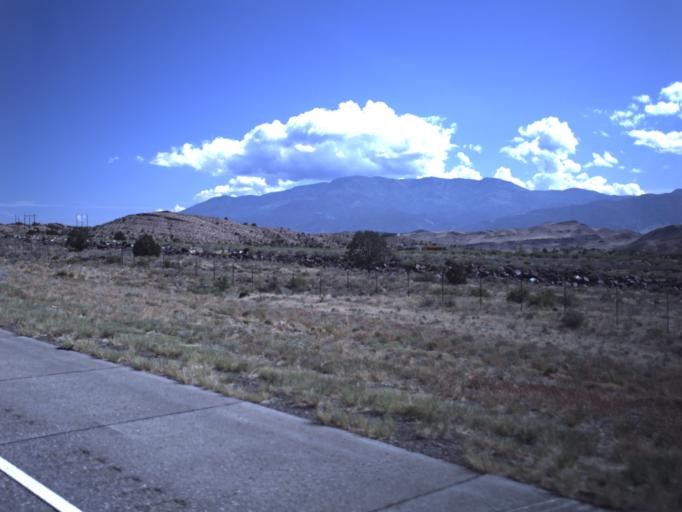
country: US
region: Utah
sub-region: Sevier County
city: Monroe
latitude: 38.5906
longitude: -112.2692
